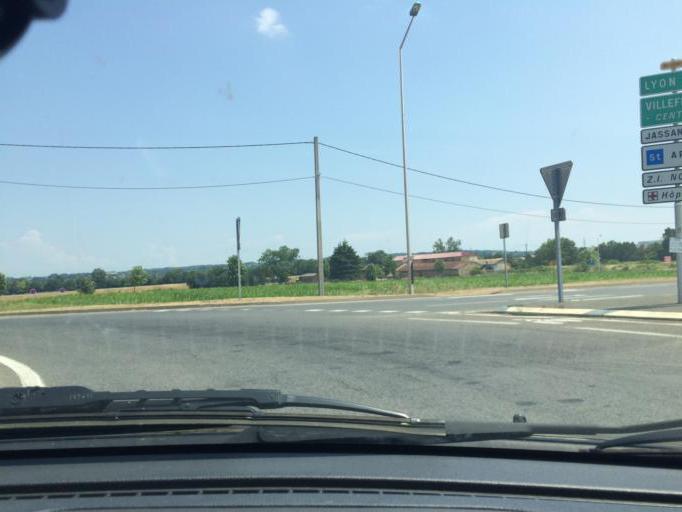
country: FR
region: Rhone-Alpes
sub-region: Departement du Rhone
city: Arnas
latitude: 46.0214
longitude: 4.7204
